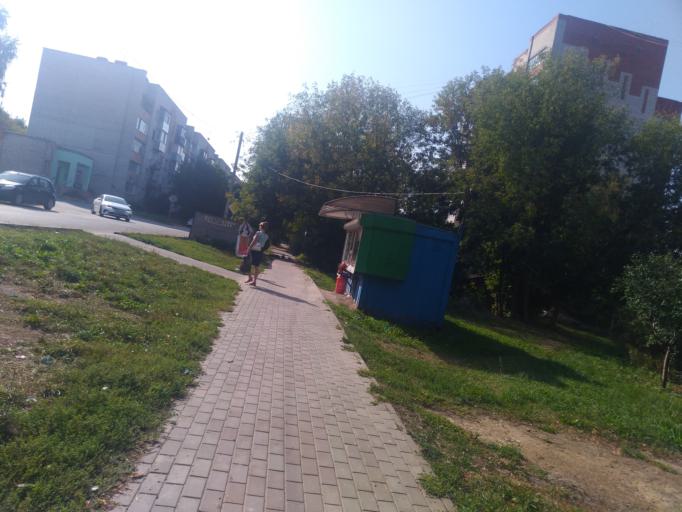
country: RU
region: Kaluga
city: Kaluga
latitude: 54.5320
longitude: 36.2534
